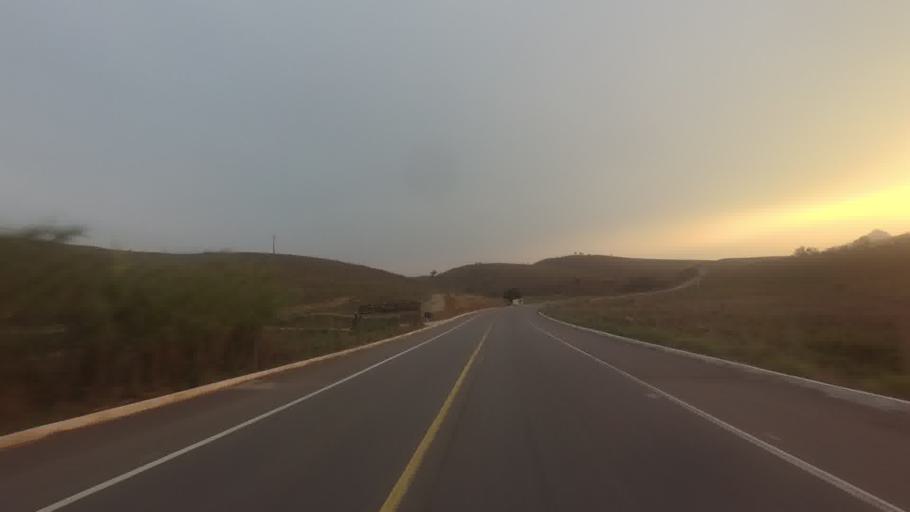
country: BR
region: Minas Gerais
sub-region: Recreio
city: Recreio
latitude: -21.7169
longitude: -42.4318
